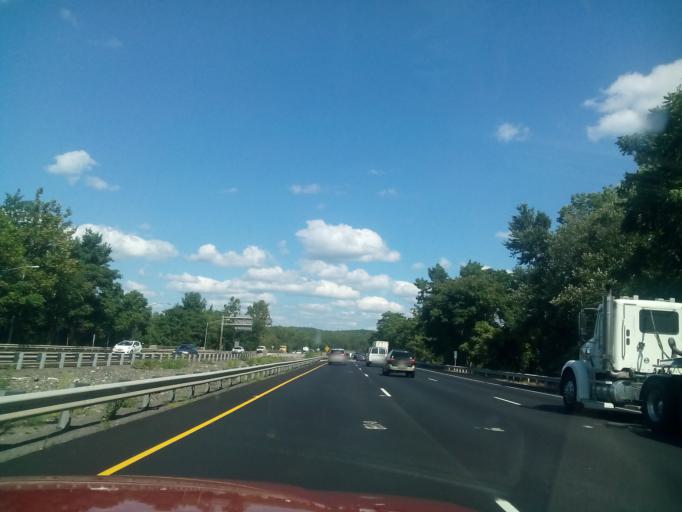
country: US
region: New Jersey
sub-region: Morris County
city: Wharton
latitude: 40.9088
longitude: -74.5733
